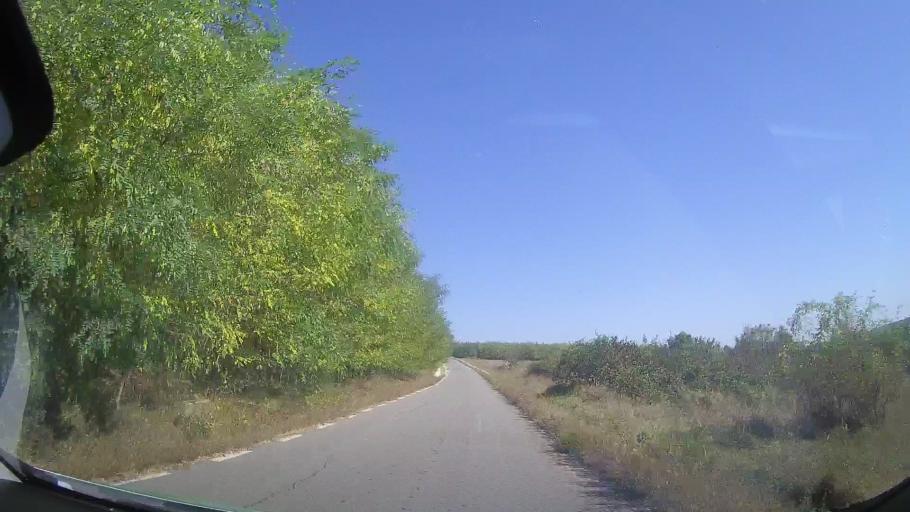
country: RO
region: Timis
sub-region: Comuna Ohaba Lunga
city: Ohaba Lunga
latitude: 45.9179
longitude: 21.9561
